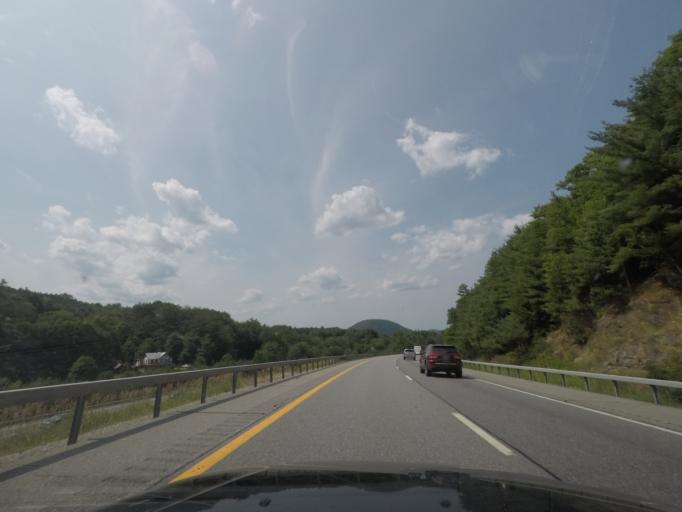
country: US
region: New York
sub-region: Warren County
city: Warrensburg
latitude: 43.4781
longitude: -73.7535
